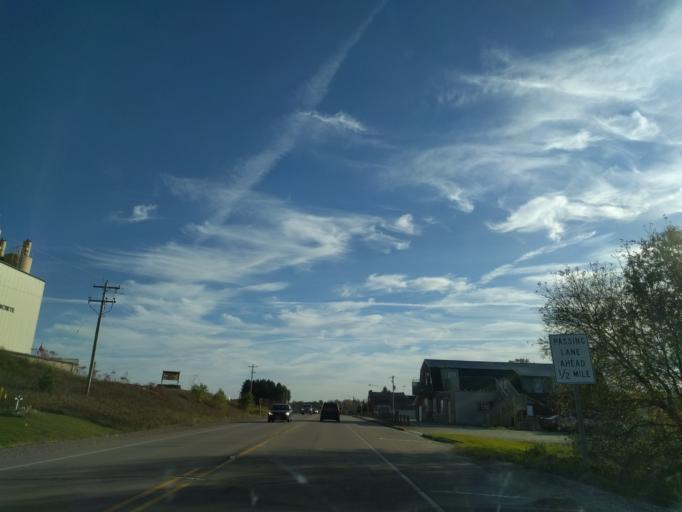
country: US
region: Wisconsin
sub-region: Marinette County
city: Peshtigo
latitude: 45.2929
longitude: -87.9921
